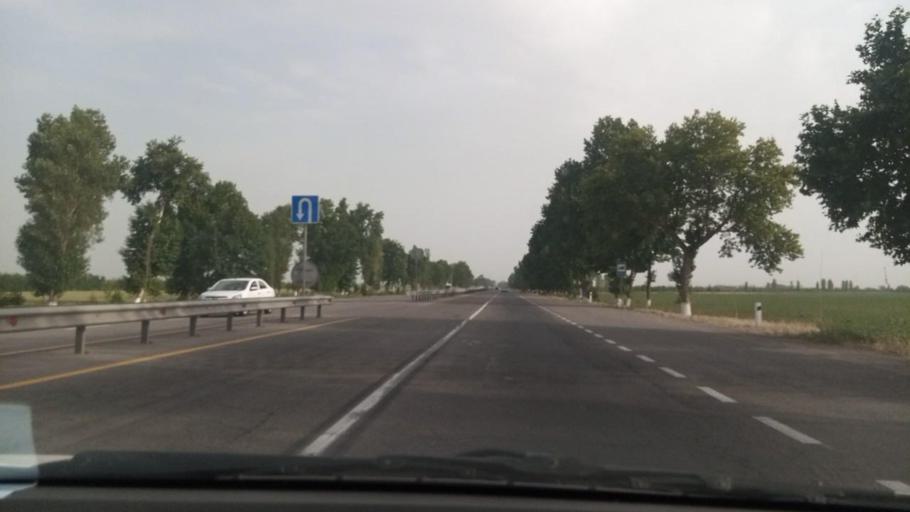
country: UZ
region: Toshkent Shahri
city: Bektemir
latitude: 41.2051
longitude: 69.4028
